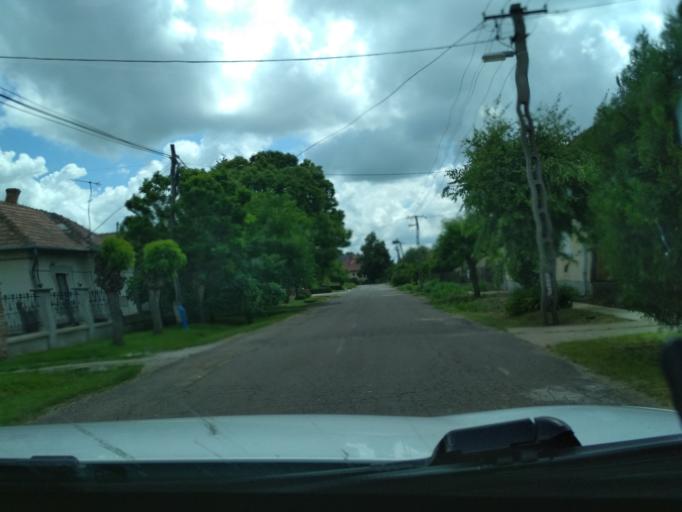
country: HU
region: Jasz-Nagykun-Szolnok
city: Tiszafured
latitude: 47.6091
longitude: 20.7523
